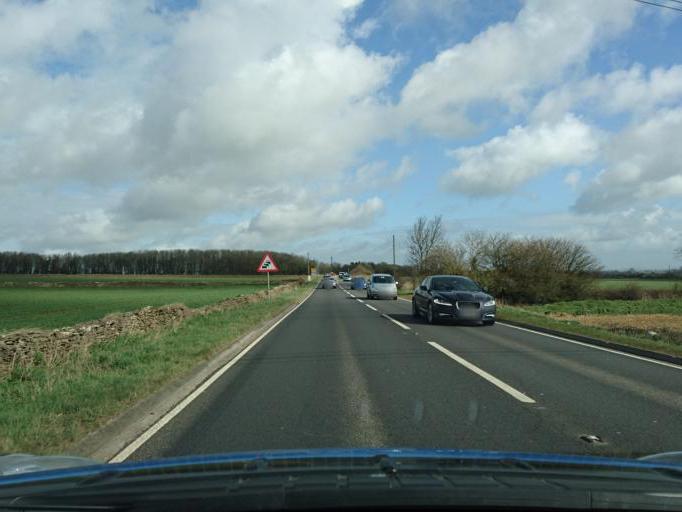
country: GB
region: England
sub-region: South Gloucestershire
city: Hinton
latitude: 51.4933
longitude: -2.3557
